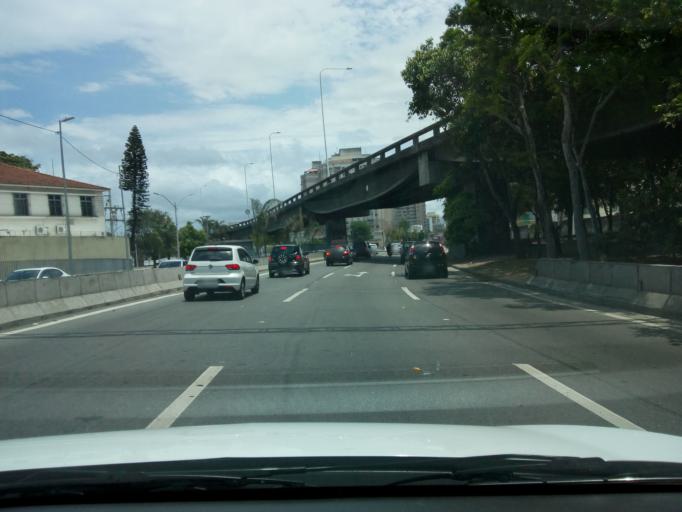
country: BR
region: Rio de Janeiro
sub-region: Niteroi
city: Niteroi
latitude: -22.8823
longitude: -43.1144
